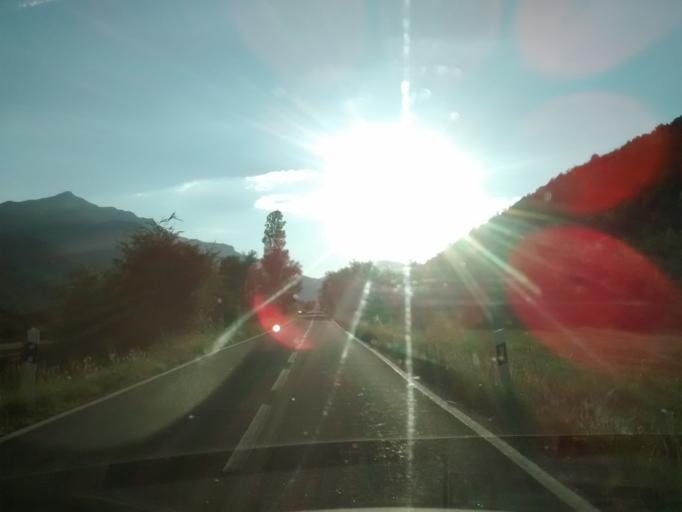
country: ES
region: Aragon
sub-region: Provincia de Huesca
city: Fiscal
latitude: 42.4754
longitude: -0.0538
